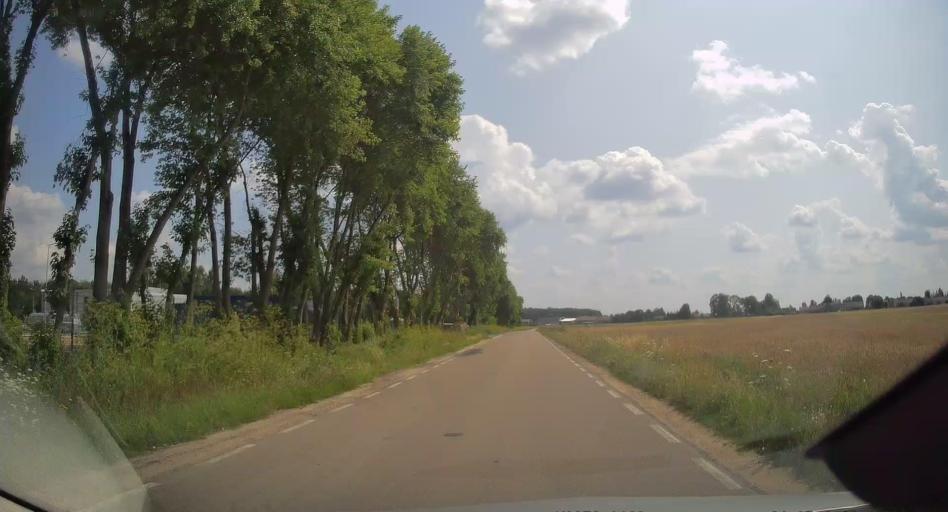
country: PL
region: Lodz Voivodeship
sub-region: Powiat tomaszowski
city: Lubochnia
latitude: 51.5745
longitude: 20.0893
